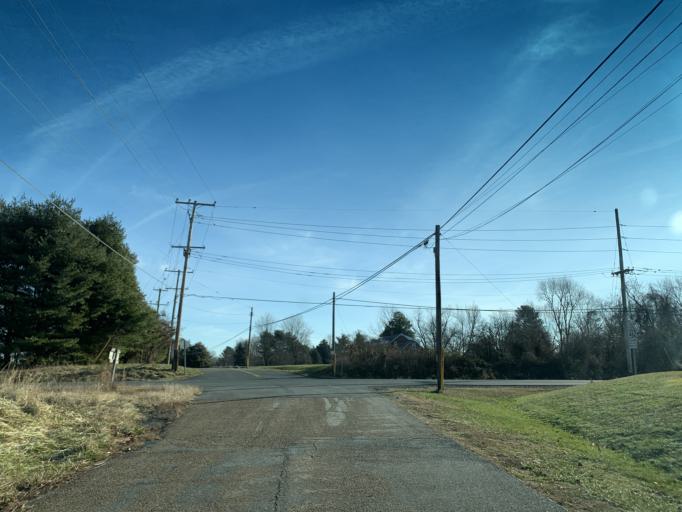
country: US
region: Maryland
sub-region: Harford County
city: Aberdeen
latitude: 39.5721
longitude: -76.1697
